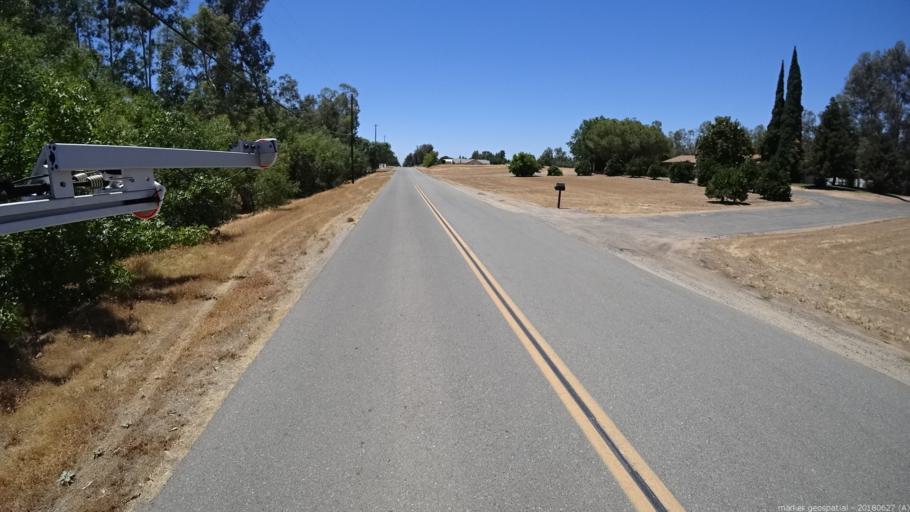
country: US
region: California
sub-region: Madera County
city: Bonadelle Ranchos-Madera Ranchos
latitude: 36.9285
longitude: -119.8627
